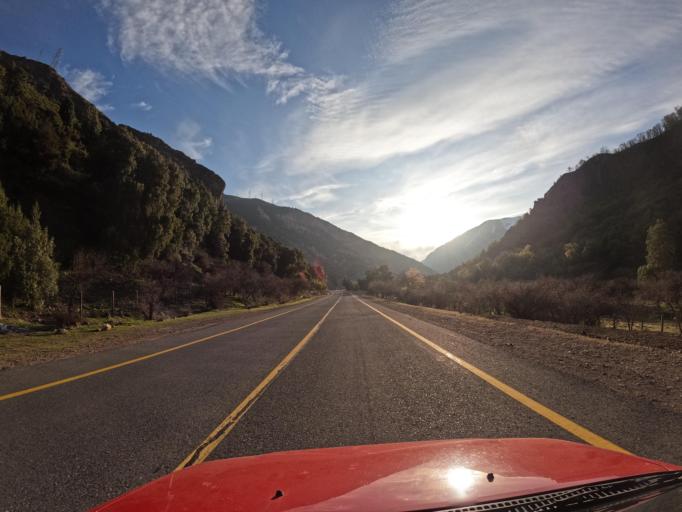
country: CL
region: Maule
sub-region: Provincia de Linares
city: Colbun
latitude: -35.8264
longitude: -70.7506
